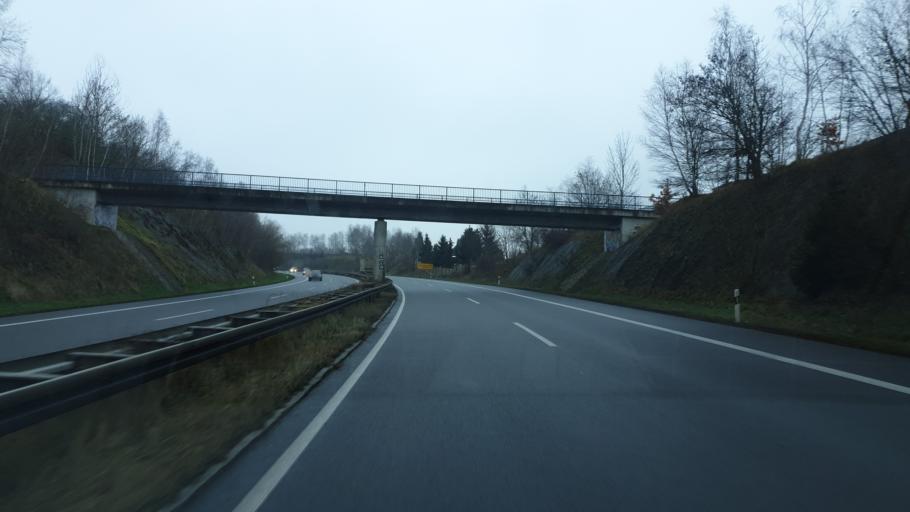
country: DE
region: Saxony
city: Zschopau
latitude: 50.7458
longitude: 13.0588
